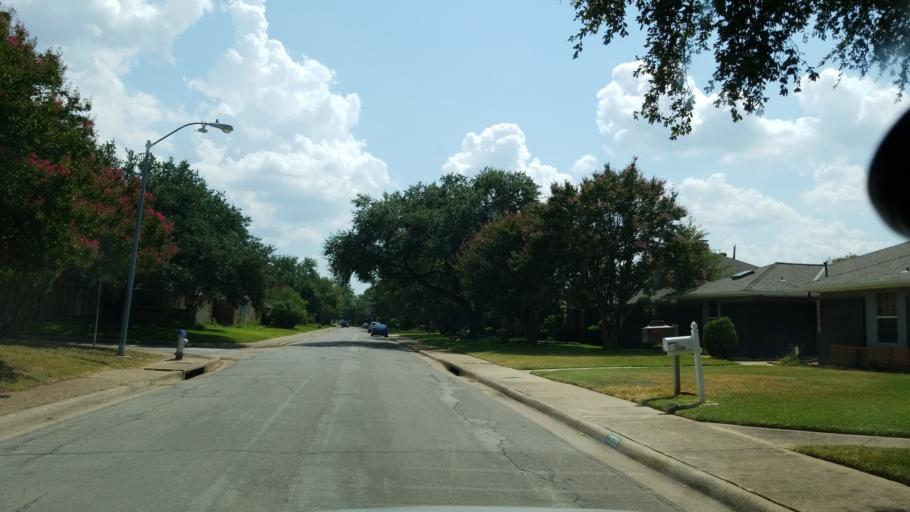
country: US
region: Texas
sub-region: Dallas County
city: Richardson
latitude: 32.9193
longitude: -96.7218
